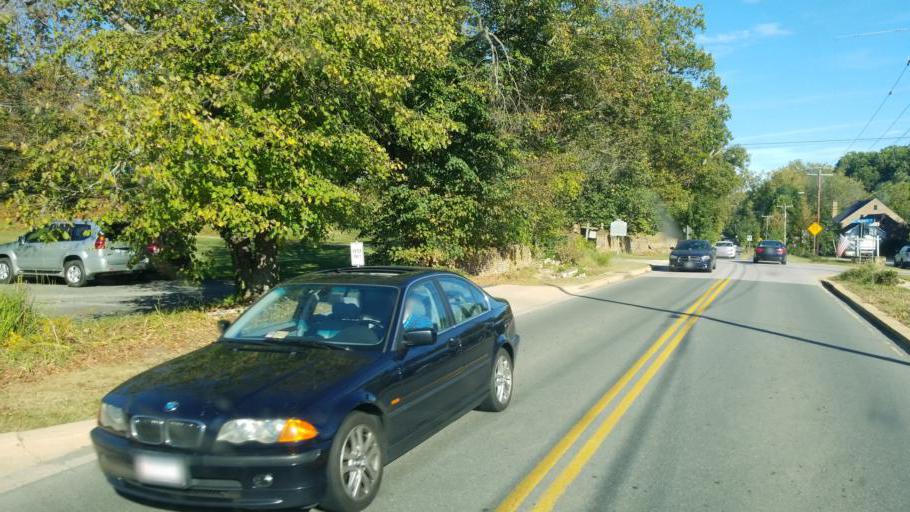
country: US
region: Virginia
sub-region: Prince William County
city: Bull Run Mountain Estates
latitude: 38.9760
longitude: -77.6434
